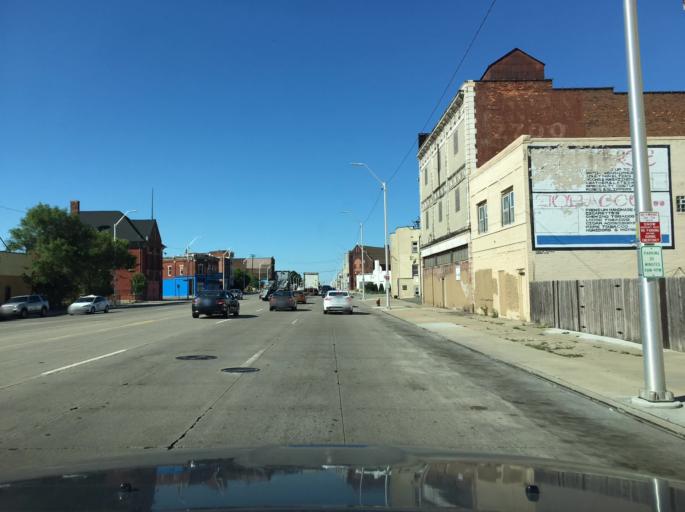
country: US
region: Michigan
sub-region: Wayne County
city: Detroit
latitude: 42.3535
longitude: -83.0313
